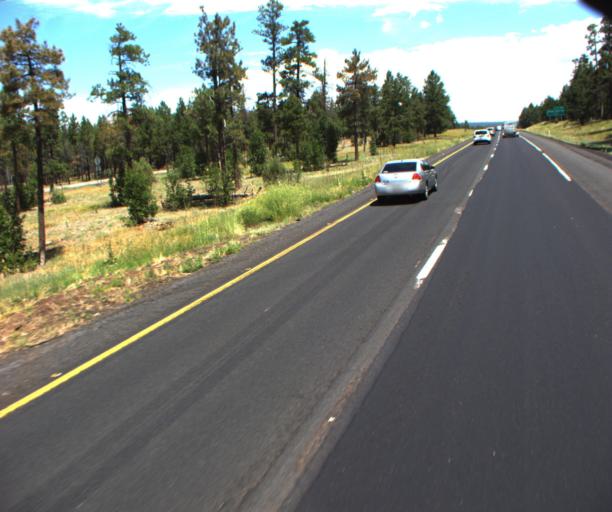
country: US
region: Arizona
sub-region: Coconino County
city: Sedona
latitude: 34.8341
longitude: -111.6049
